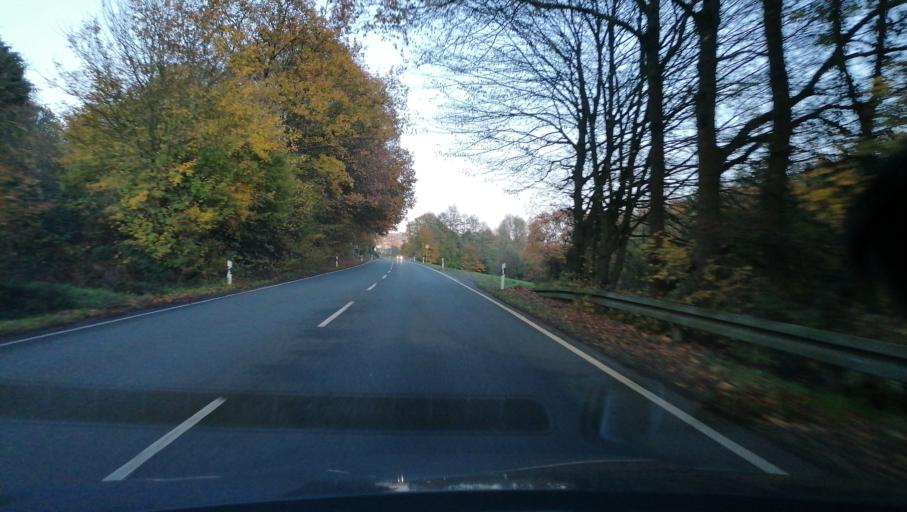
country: DE
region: North Rhine-Westphalia
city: Wetter (Ruhr)
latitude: 51.4077
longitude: 7.3903
